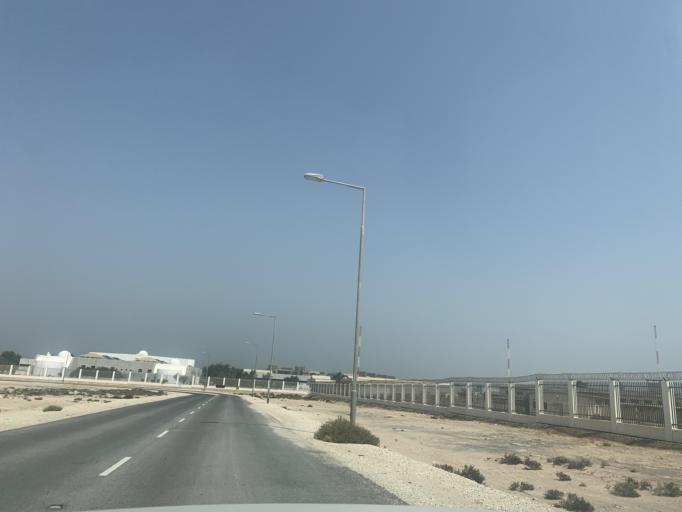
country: BH
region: Central Governorate
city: Madinat Hamad
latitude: 26.1568
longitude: 50.4735
